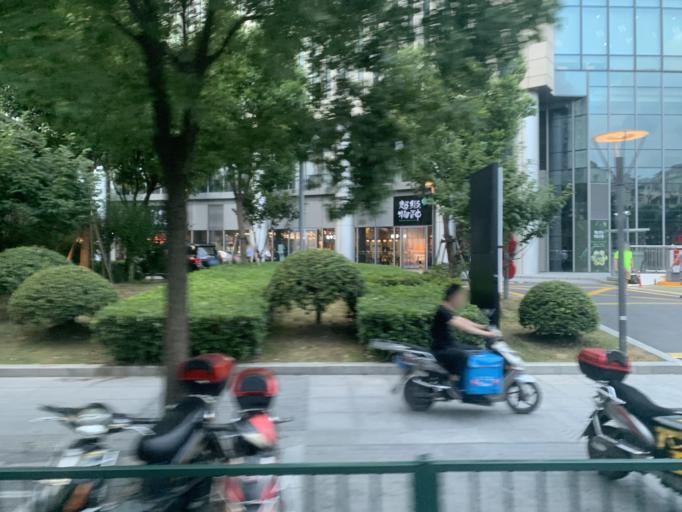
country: CN
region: Shanghai Shi
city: Pudong
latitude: 31.2319
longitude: 121.5244
